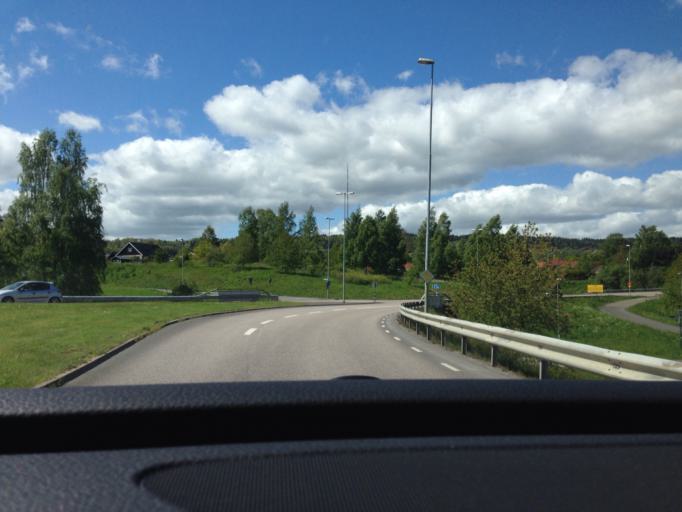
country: SE
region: Vaestra Goetaland
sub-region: Skovde Kommun
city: Skoevde
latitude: 58.4081
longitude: 13.8535
